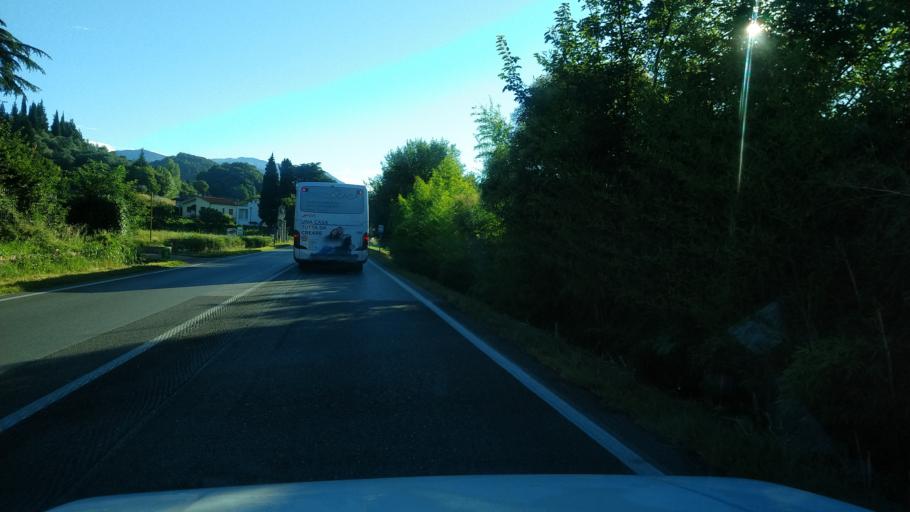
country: IT
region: Veneto
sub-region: Provincia di Vicenza
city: Marostica
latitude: 45.7543
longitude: 11.6798
